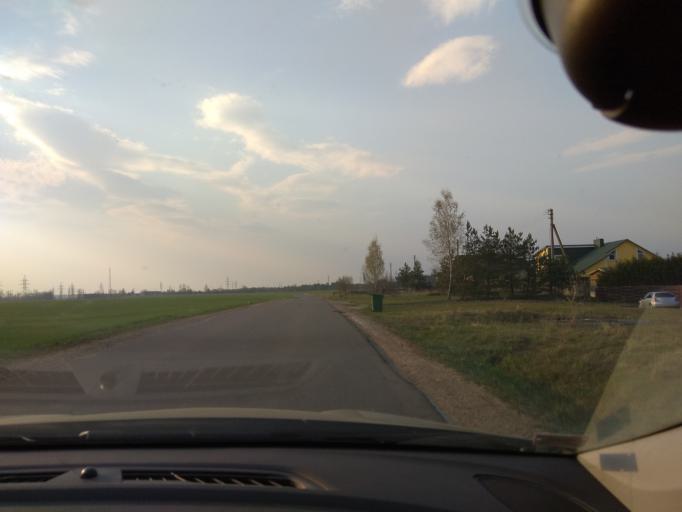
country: LT
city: Baltoji Voke
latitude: 54.6063
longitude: 25.1315
